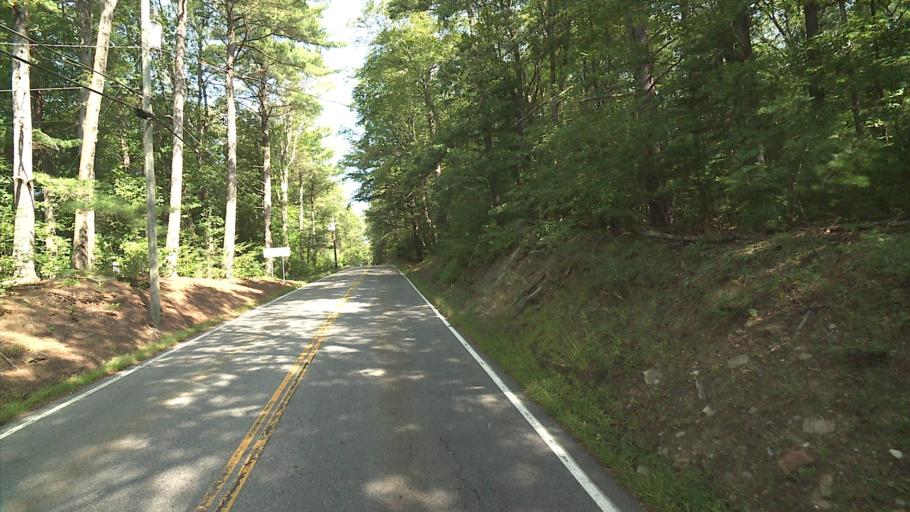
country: US
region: Connecticut
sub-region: Windham County
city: Quinebaug
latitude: 41.9966
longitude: -71.9994
